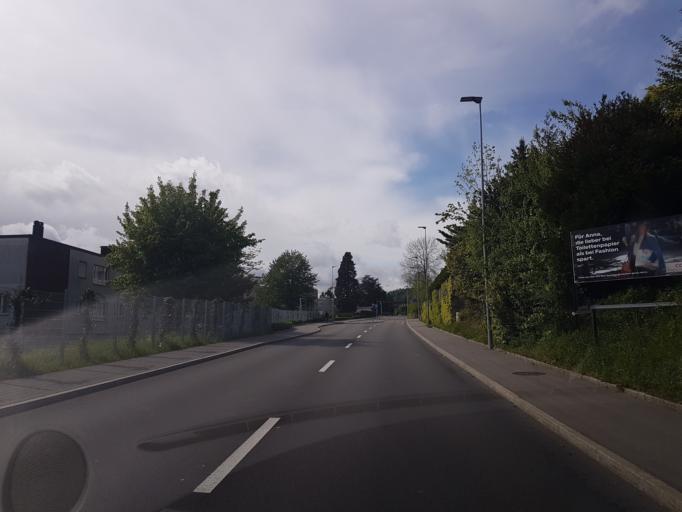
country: CH
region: Zurich
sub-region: Bezirk Dietikon
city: Geroldswil
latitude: 47.4230
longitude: 8.4045
